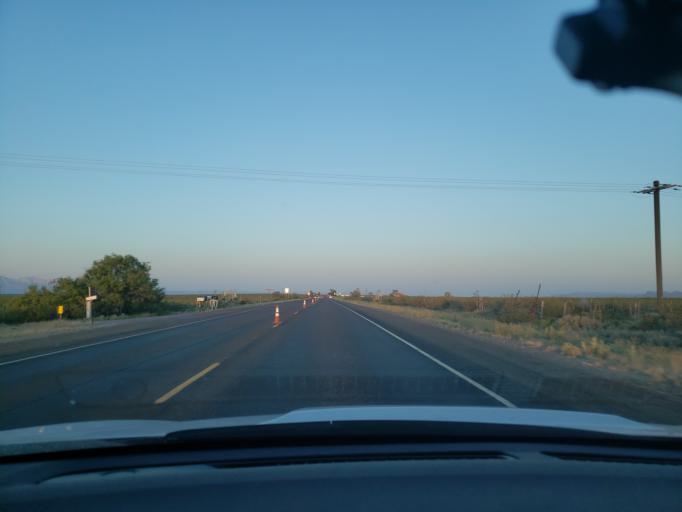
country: US
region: Texas
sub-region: Hudspeth County
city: Sierra Blanca
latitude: 31.7624
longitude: -105.3734
